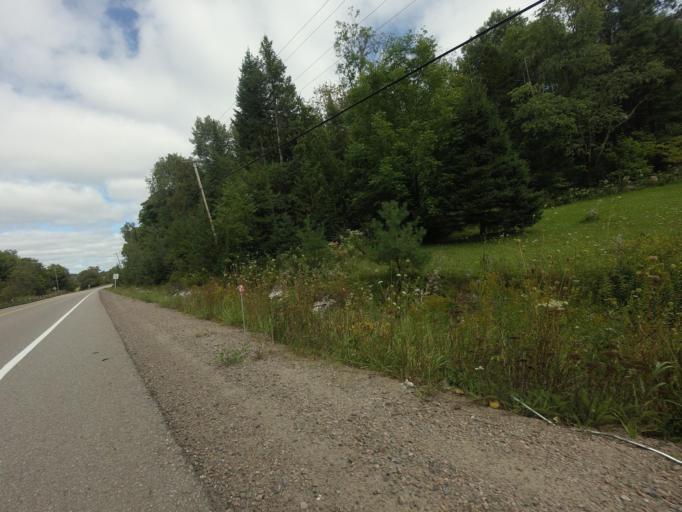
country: CA
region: Ontario
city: Bancroft
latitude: 44.9677
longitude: -78.2804
